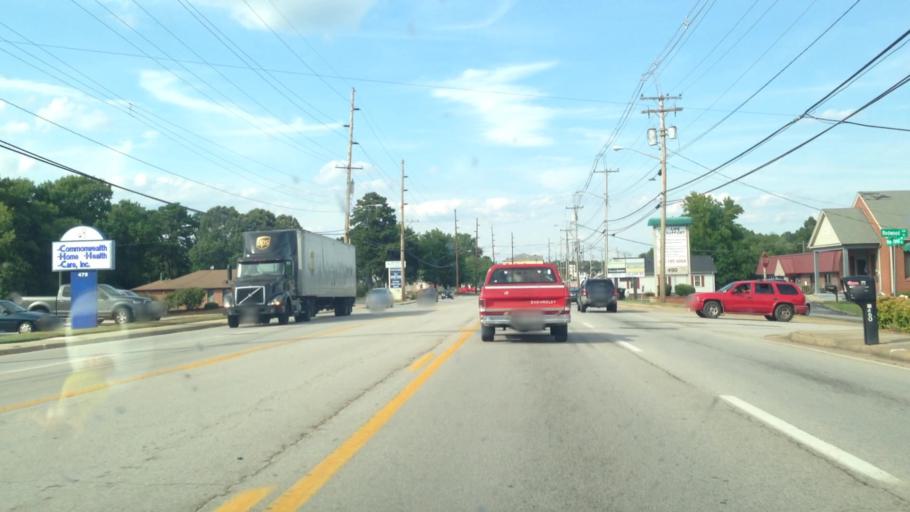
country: US
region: Virginia
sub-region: City of Danville
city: Danville
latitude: 36.6059
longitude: -79.4108
